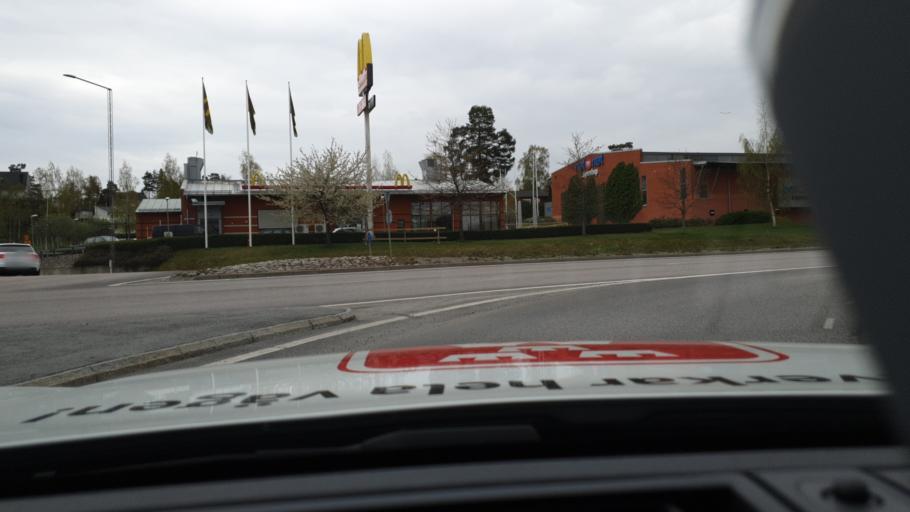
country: SE
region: Stockholm
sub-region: Haninge Kommun
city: Haninge
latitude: 59.1775
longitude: 18.1482
